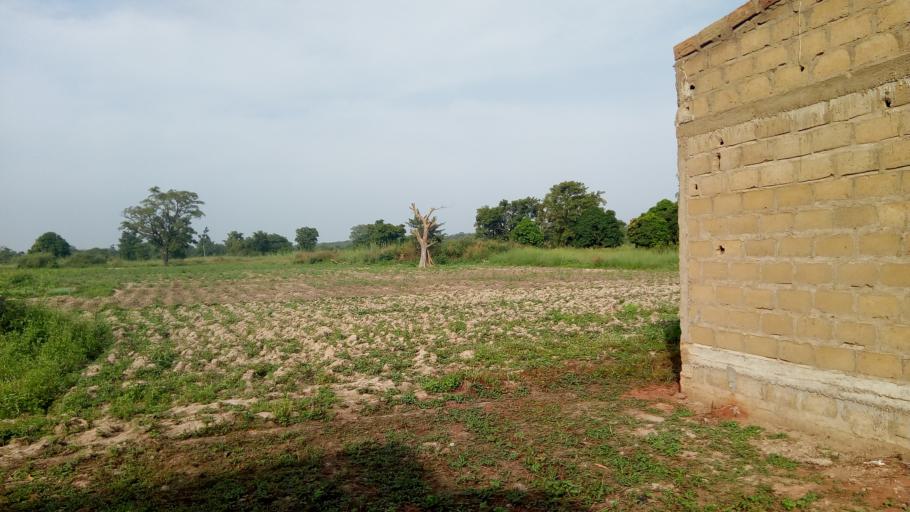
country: ML
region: Koulikoro
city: Kangaba
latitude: 11.6626
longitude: -8.7307
